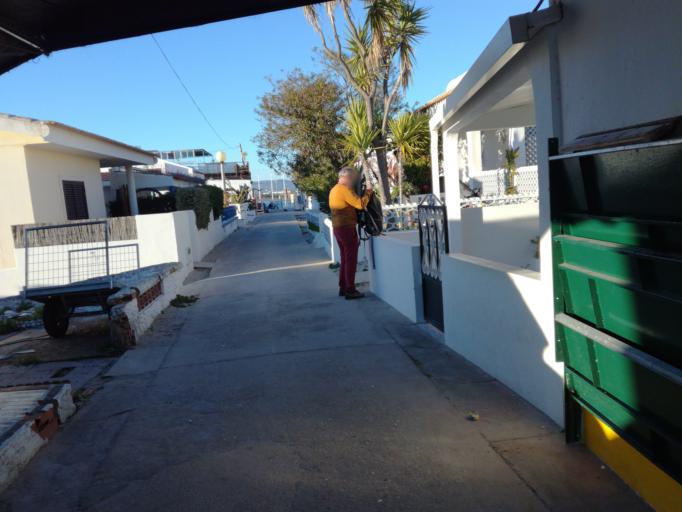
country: PT
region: Faro
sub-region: Olhao
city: Olhao
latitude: 37.0224
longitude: -7.8057
